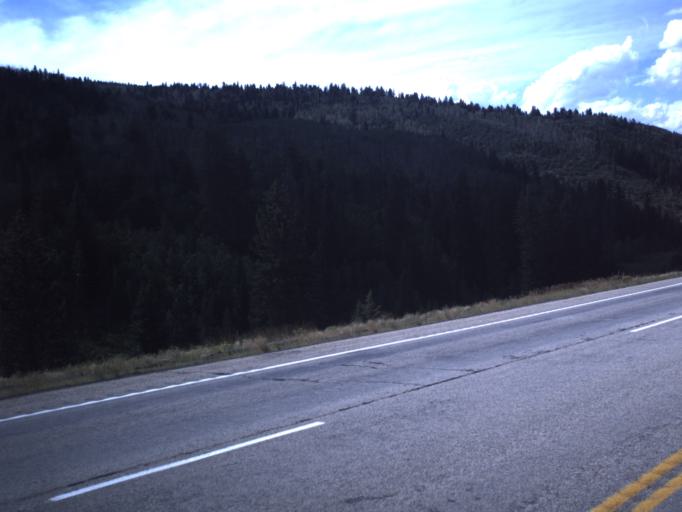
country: US
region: Utah
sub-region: Wasatch County
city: Heber
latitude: 40.3183
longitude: -111.2583
